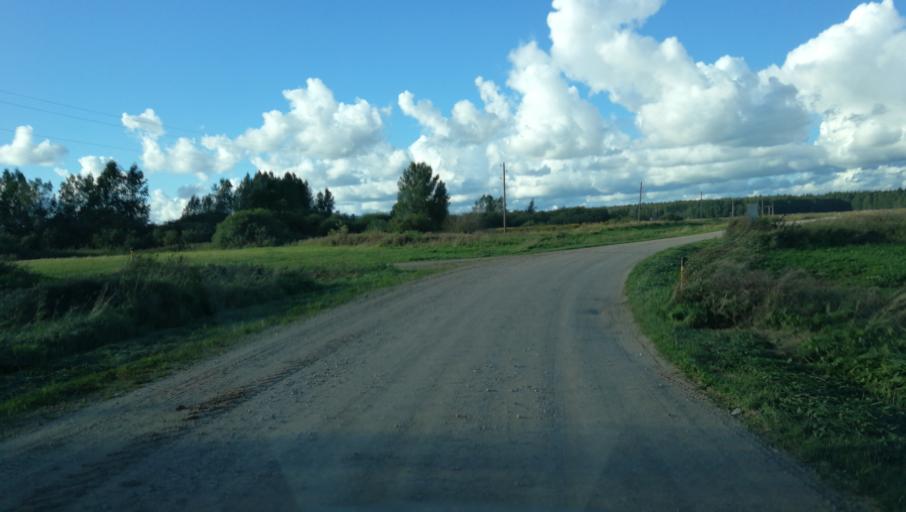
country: LV
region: Riga
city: Jaunciems
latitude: 57.0797
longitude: 24.2275
